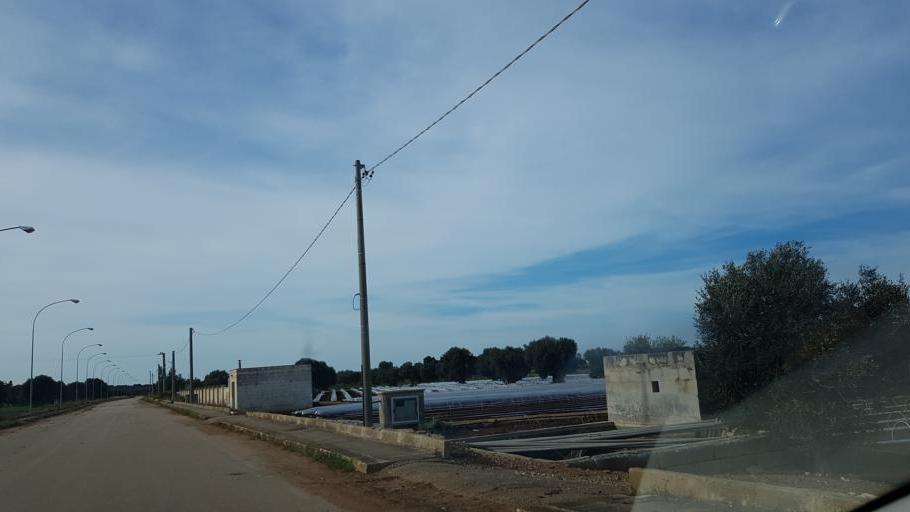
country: IT
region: Apulia
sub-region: Provincia di Brindisi
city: Fasano
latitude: 40.8938
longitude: 17.3637
